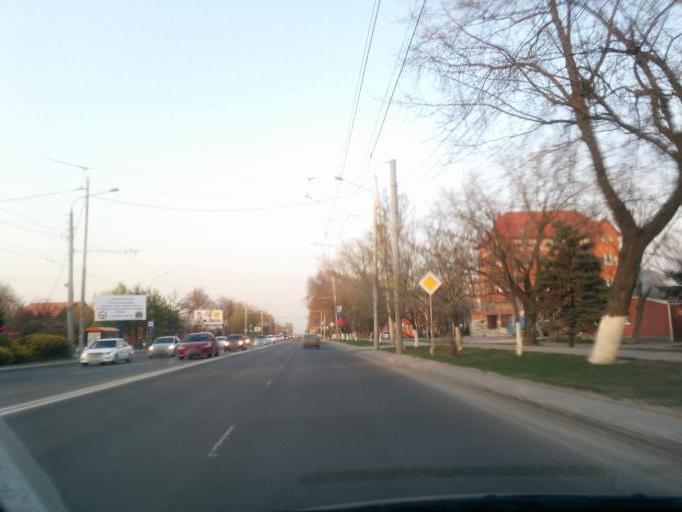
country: RU
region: Rostov
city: Imeni Chkalova
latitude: 47.2455
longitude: 39.7703
